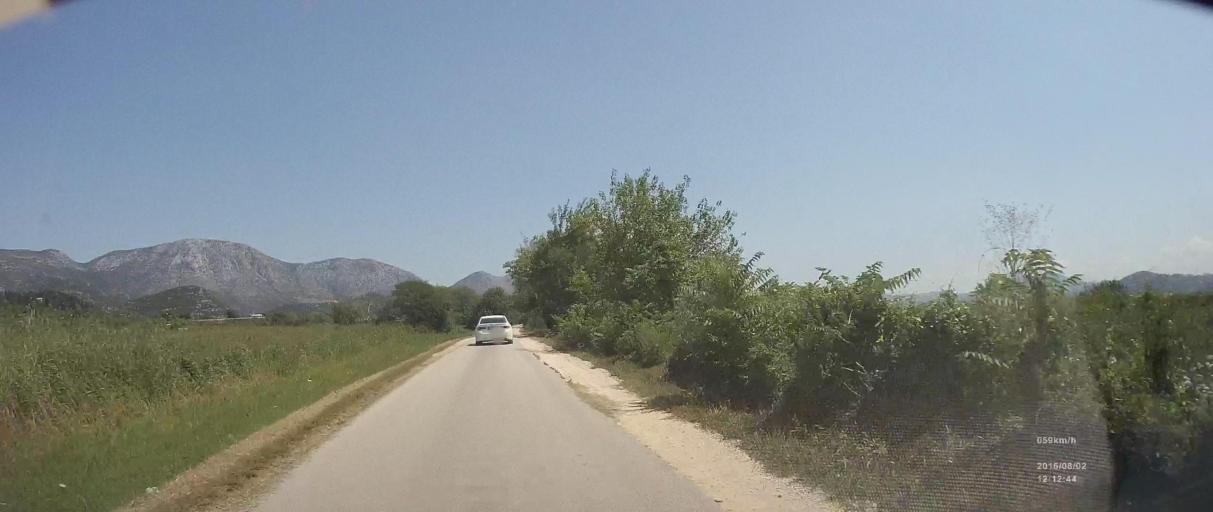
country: HR
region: Dubrovacko-Neretvanska
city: Komin
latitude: 43.0351
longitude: 17.4756
